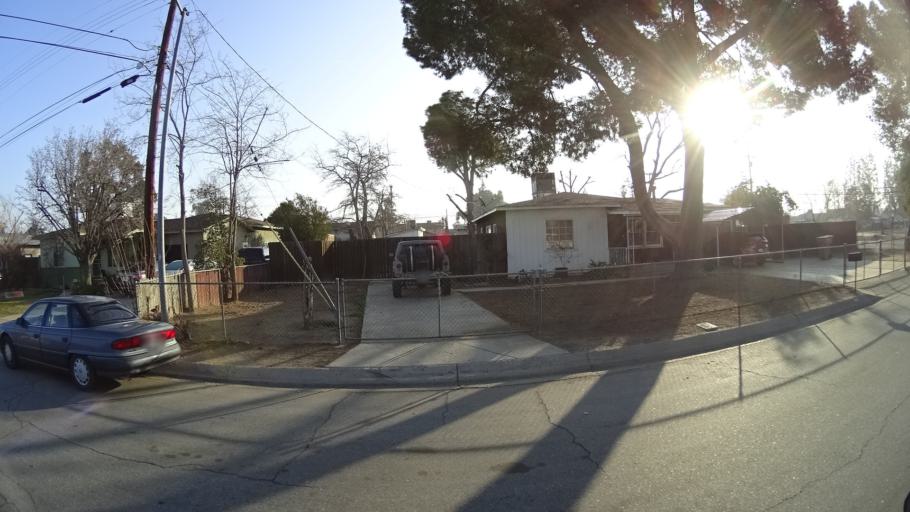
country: US
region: California
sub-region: Kern County
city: Bakersfield
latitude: 35.3628
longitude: -119.0445
